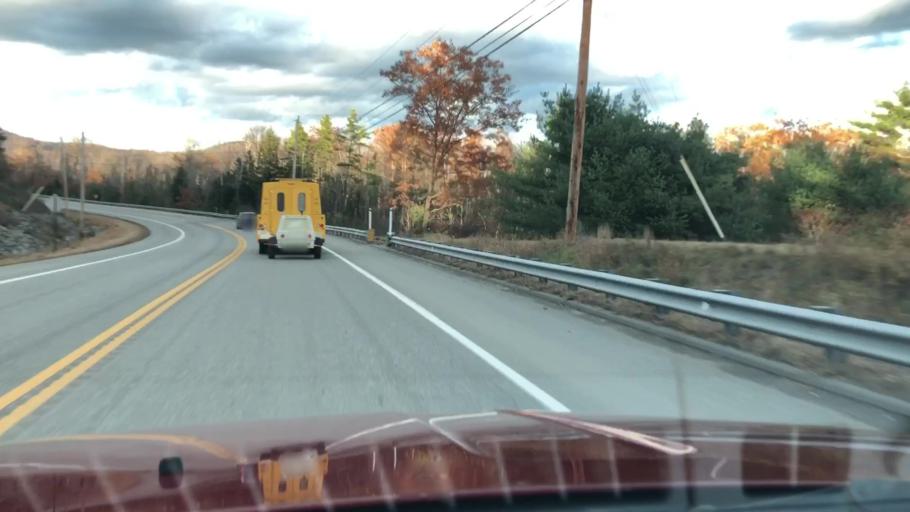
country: US
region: Maine
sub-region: Oxford County
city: Peru
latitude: 44.5303
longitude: -70.4057
